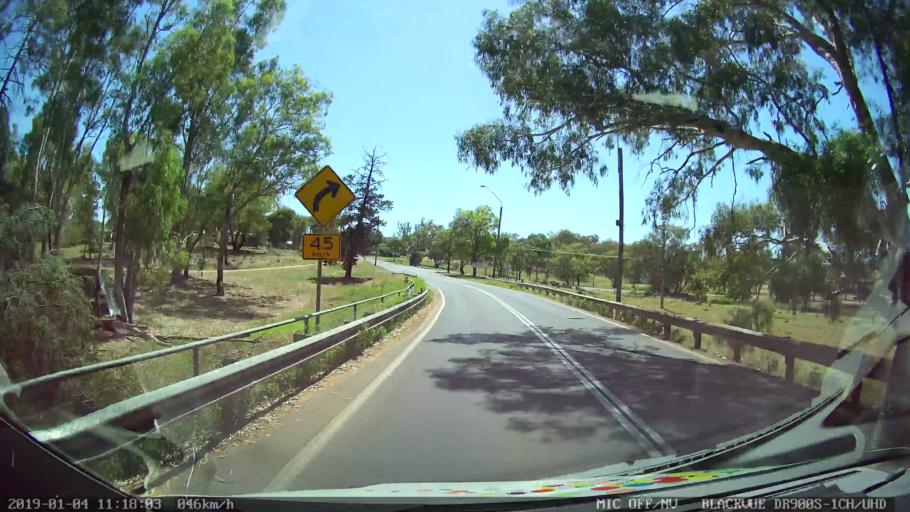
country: AU
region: New South Wales
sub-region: Cabonne
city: Molong
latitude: -33.1858
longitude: 148.6998
